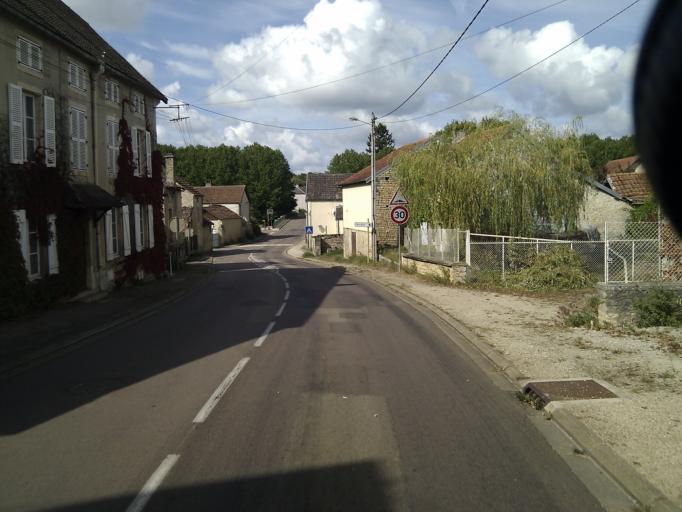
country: FR
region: Bourgogne
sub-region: Departement de la Cote-d'Or
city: Chatillon-sur-Seine
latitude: 47.9154
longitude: 4.6674
